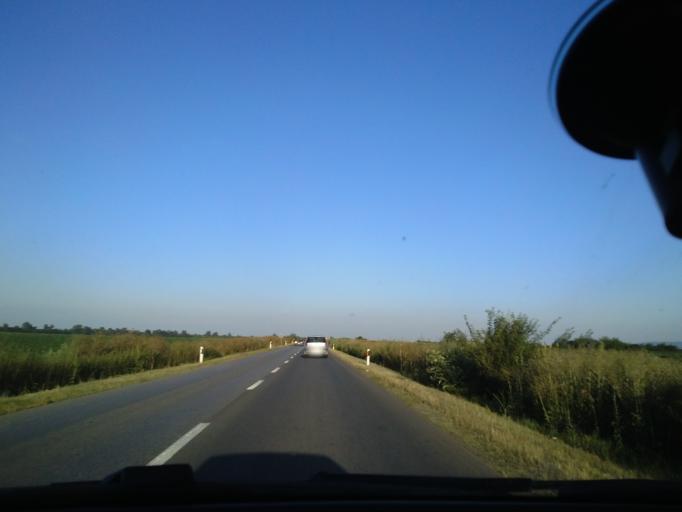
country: RS
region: Autonomna Pokrajina Vojvodina
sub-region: Juznobacki Okrug
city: Backi Petrovac
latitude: 45.3442
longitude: 19.6370
